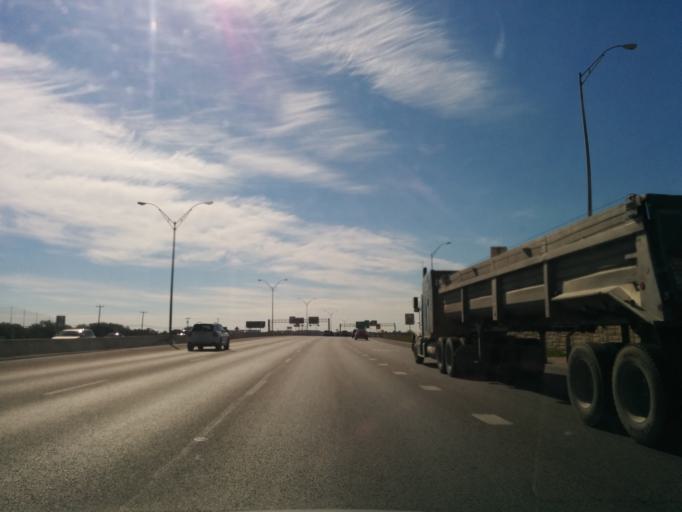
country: US
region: Texas
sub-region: Bexar County
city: Shavano Park
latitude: 29.5998
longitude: -98.6001
